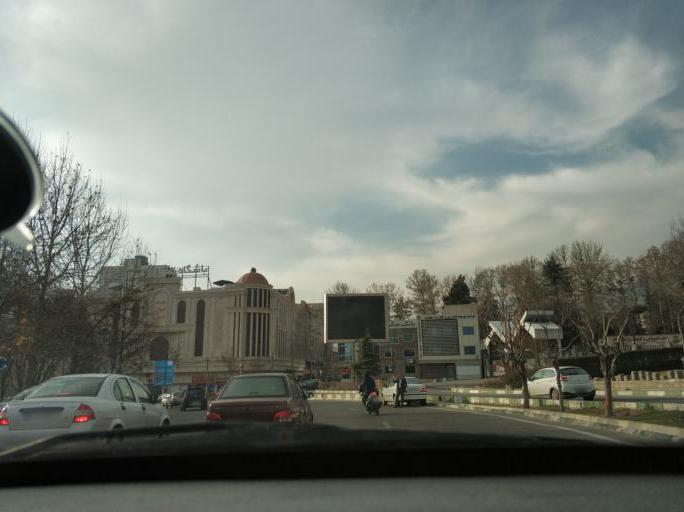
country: IR
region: Tehran
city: Tajrish
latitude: 35.8021
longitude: 51.4874
